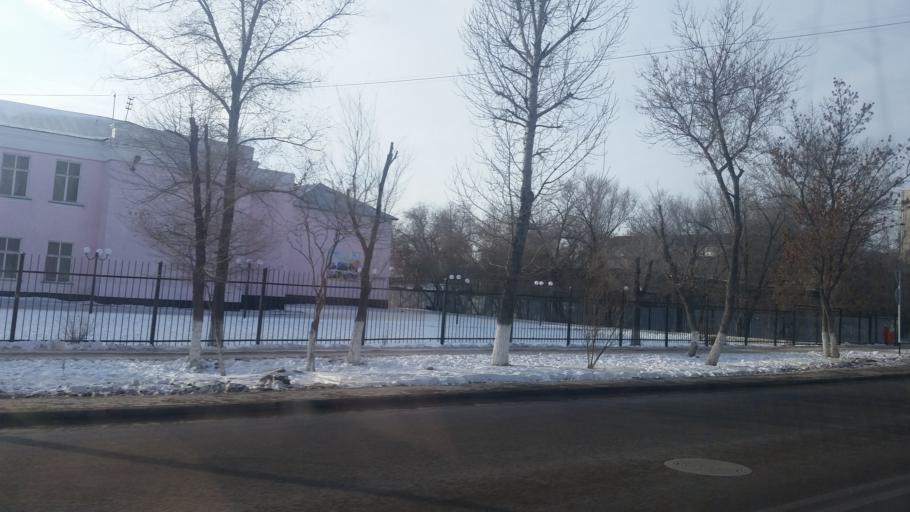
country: KZ
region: Astana Qalasy
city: Astana
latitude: 51.1964
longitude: 71.3997
